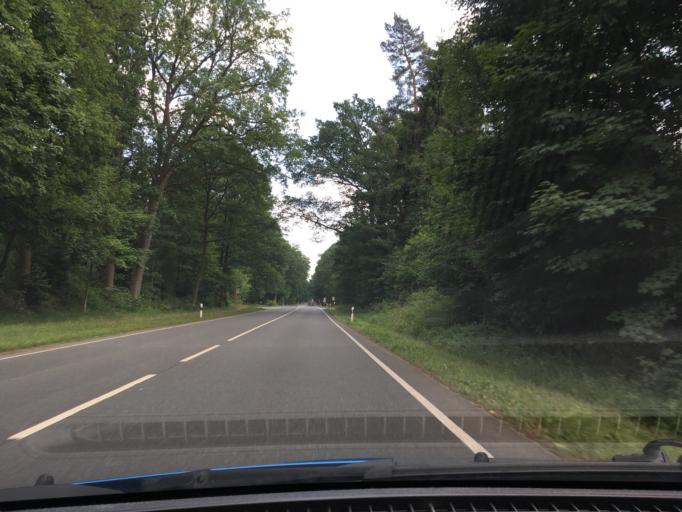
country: DE
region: Lower Saxony
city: Kakenstorf
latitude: 53.2890
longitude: 9.7931
